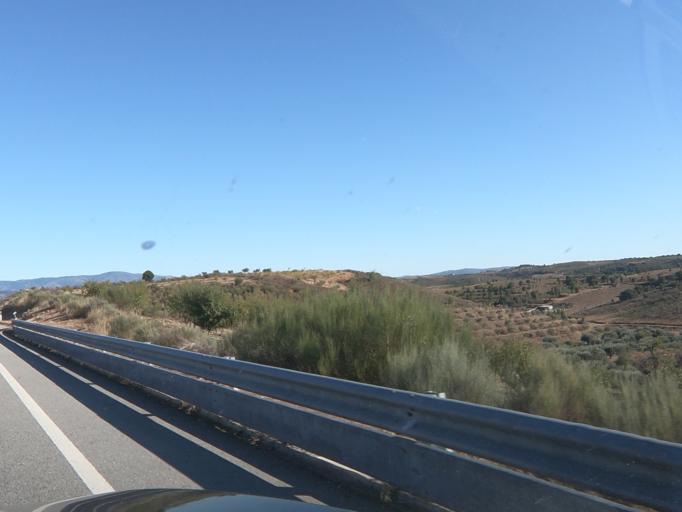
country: PT
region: Braganca
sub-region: Mirandela
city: Mirandela
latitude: 41.5191
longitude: -7.2351
